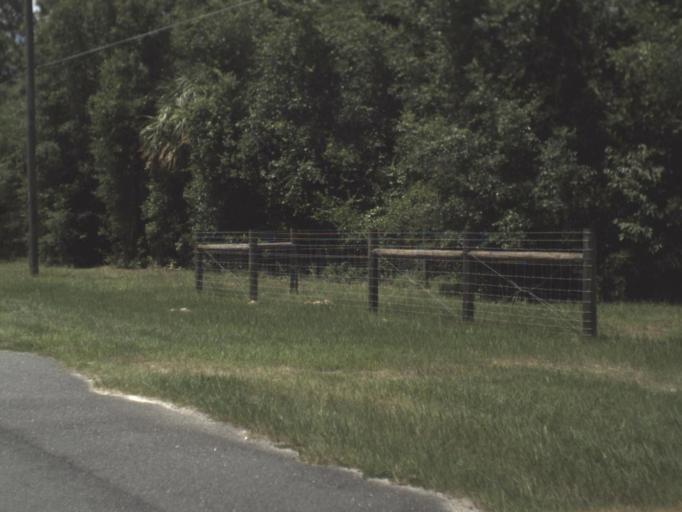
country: US
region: Florida
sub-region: Alachua County
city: Hawthorne
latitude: 29.6355
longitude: -82.0310
